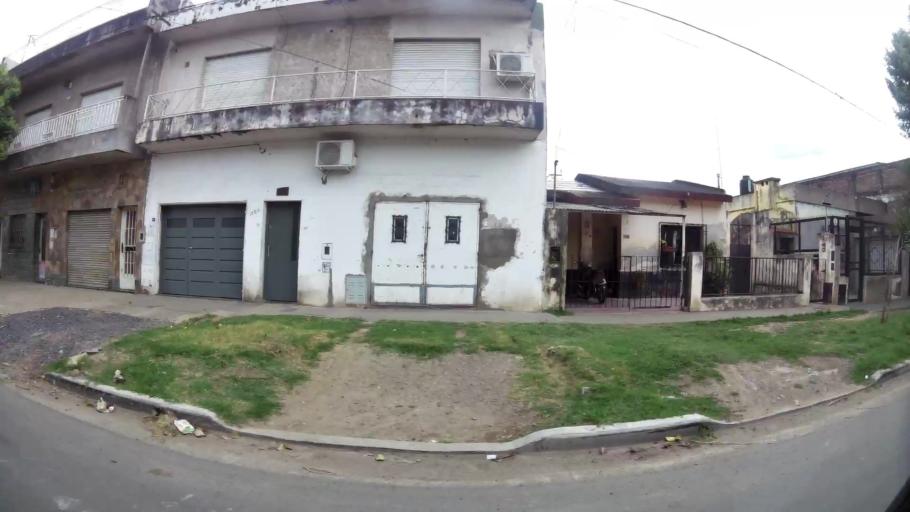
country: AR
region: Santa Fe
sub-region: Departamento de Rosario
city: Rosario
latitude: -32.9810
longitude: -60.6560
